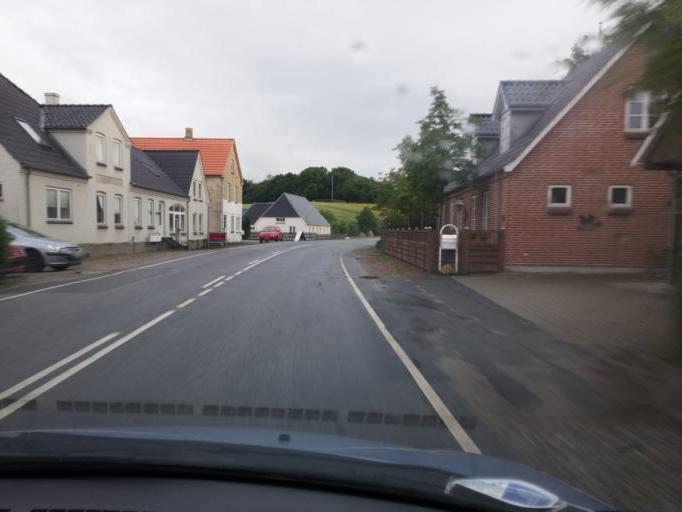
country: DK
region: South Denmark
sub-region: Kerteminde Kommune
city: Kerteminde
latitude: 55.5156
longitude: 10.6549
